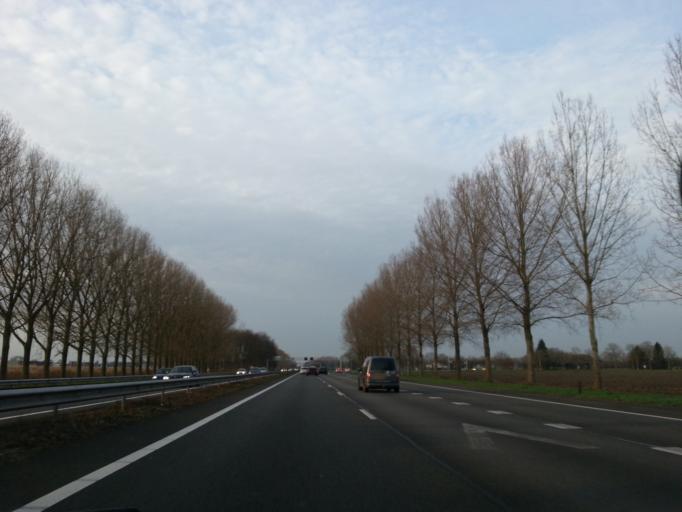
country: NL
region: Gelderland
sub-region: Gemeente Zevenaar
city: Zevenaar
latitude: 51.9361
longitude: 6.0955
